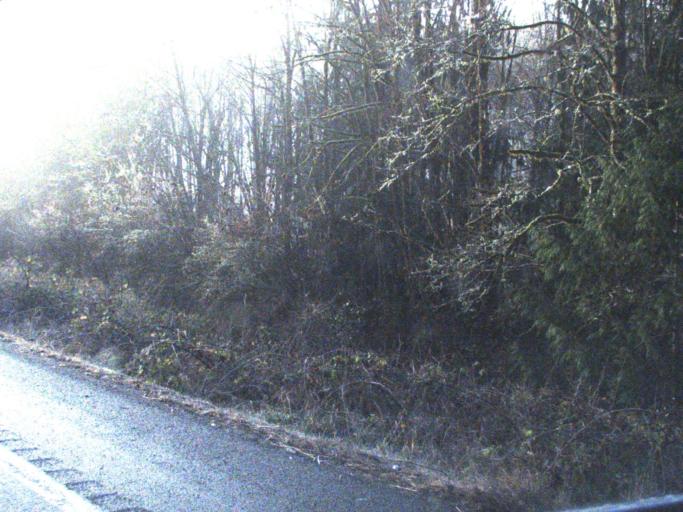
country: US
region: Washington
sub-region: Snohomish County
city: Darrington
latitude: 48.5278
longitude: -121.7171
